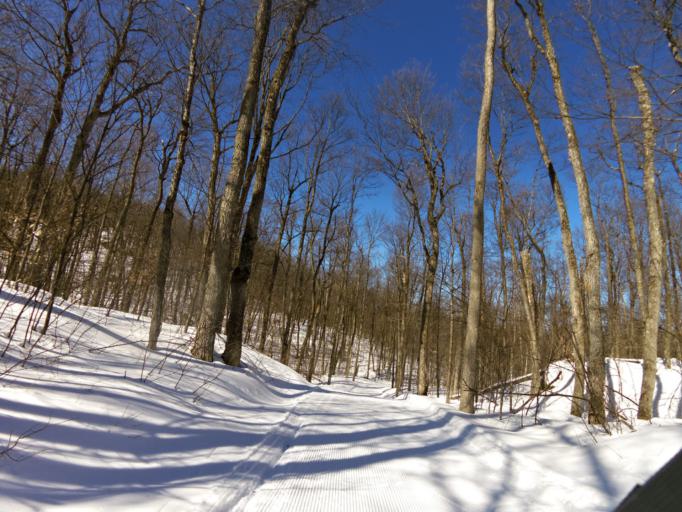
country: CA
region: Quebec
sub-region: Outaouais
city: Wakefield
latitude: 45.5055
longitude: -75.8686
